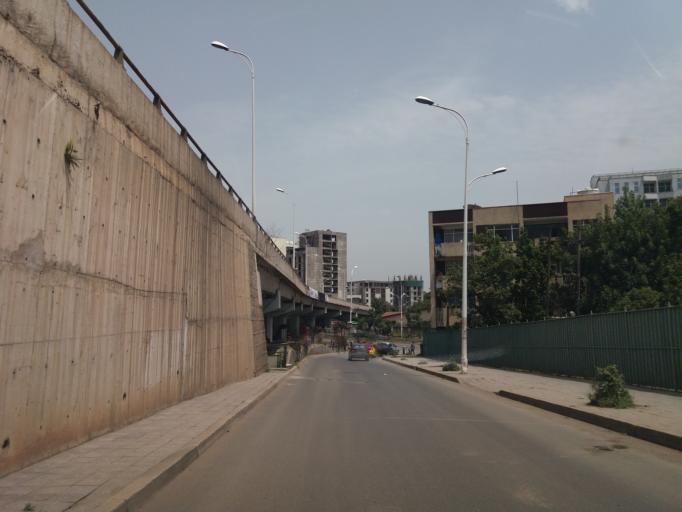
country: ET
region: Adis Abeba
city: Addis Ababa
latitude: 8.9933
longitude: 38.7786
